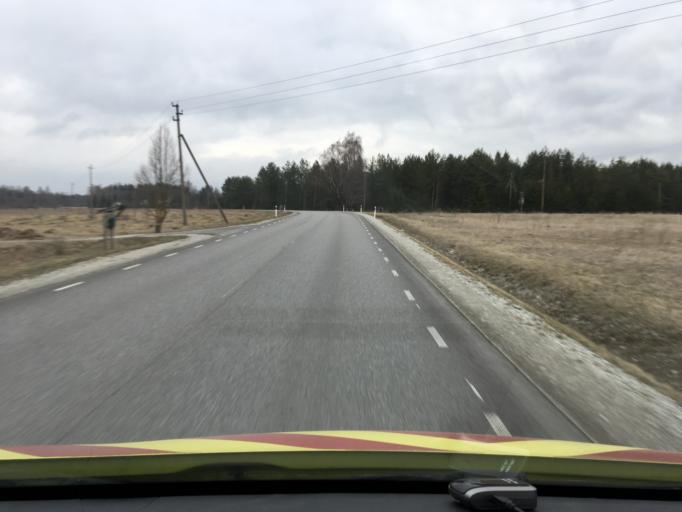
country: EE
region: Raplamaa
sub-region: Rapla vald
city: Rapla
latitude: 59.0057
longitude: 24.8424
